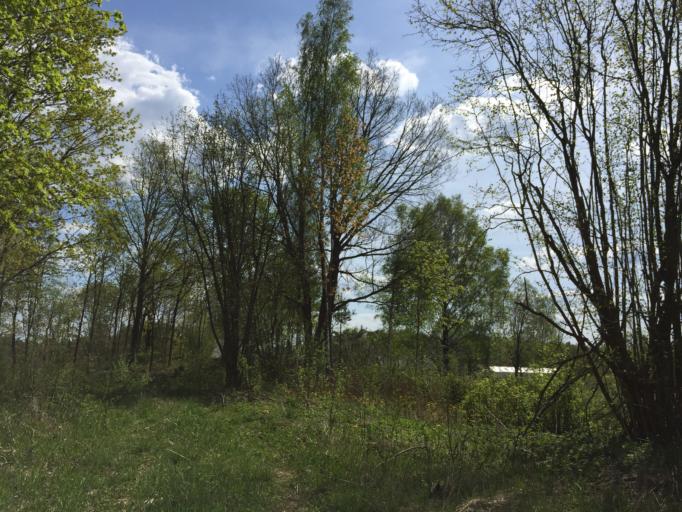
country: LV
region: Limbazu Rajons
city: Limbazi
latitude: 57.3530
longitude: 24.6580
